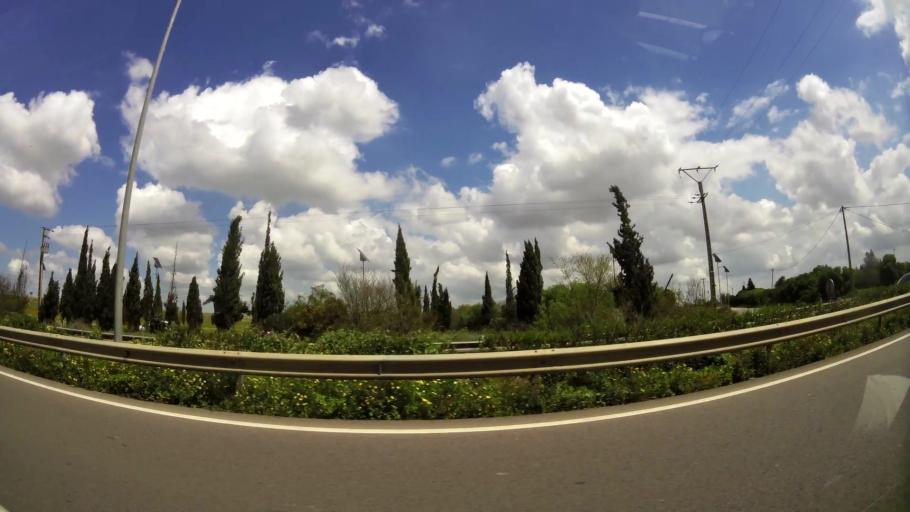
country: MA
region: Chaouia-Ouardigha
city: Nouaseur
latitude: 33.3949
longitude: -7.6205
